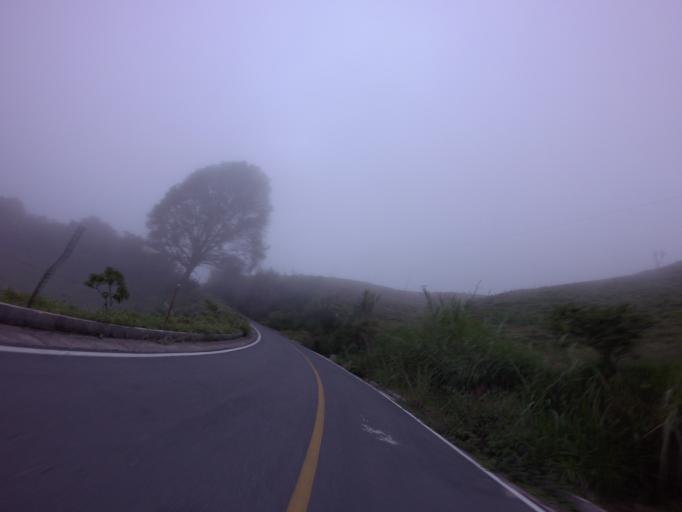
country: CO
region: Caldas
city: Manzanares
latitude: 5.3353
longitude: -75.1188
